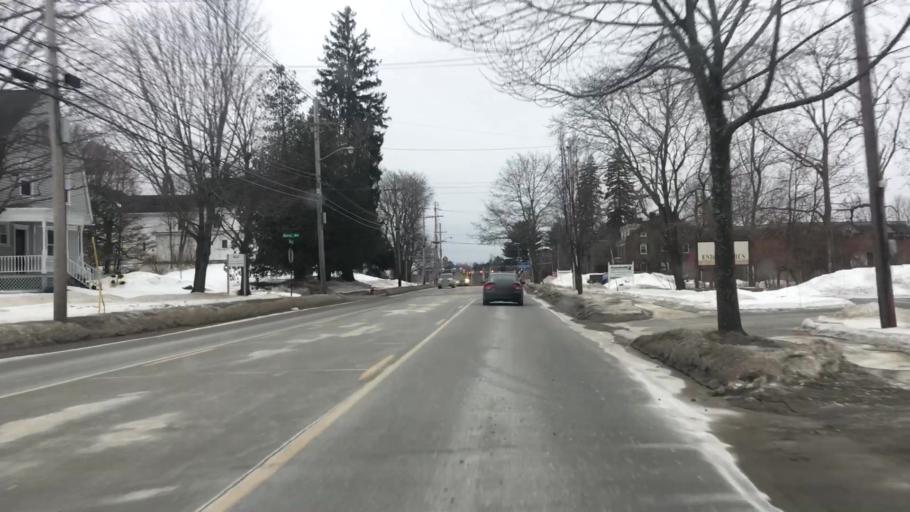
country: US
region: Maine
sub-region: Androscoggin County
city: Lewiston
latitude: 44.1173
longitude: -70.2054
